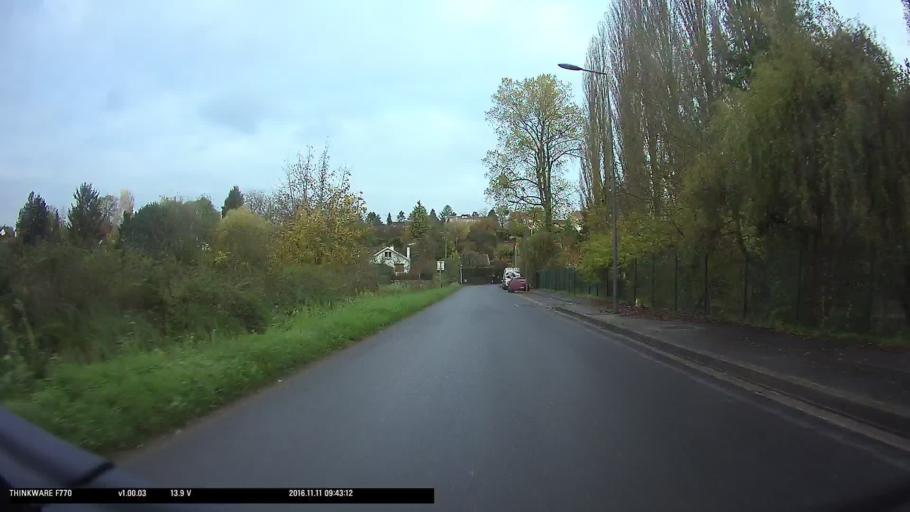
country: FR
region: Ile-de-France
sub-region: Departement du Val-d'Oise
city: Osny
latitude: 49.0665
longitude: 2.0505
